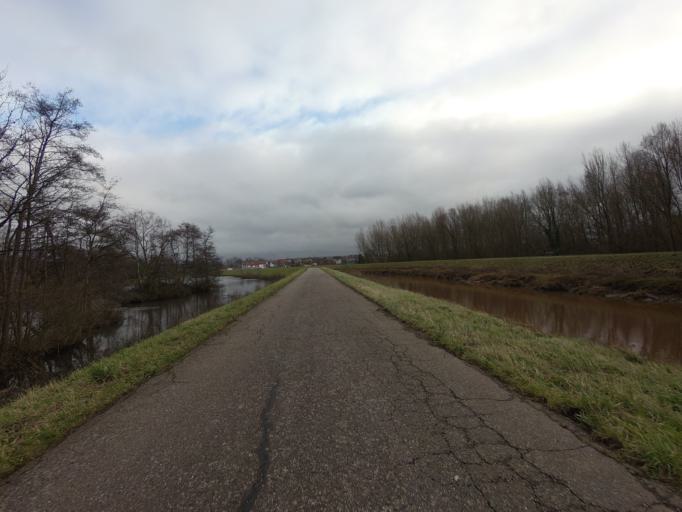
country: BE
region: Flanders
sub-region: Provincie Antwerpen
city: Lier
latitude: 51.1333
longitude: 4.5841
